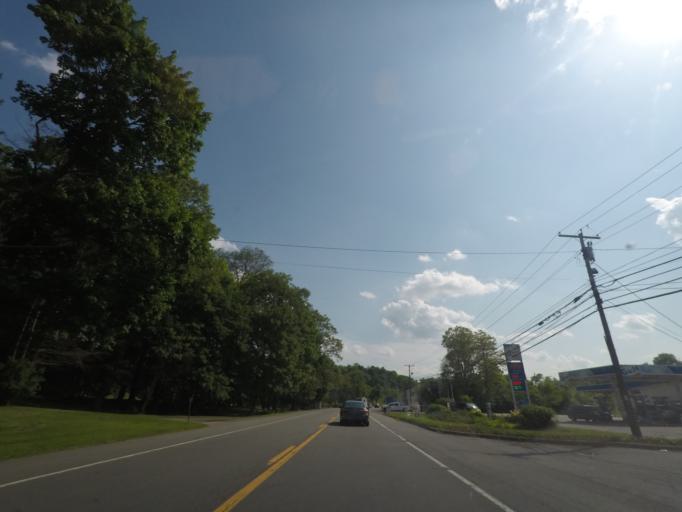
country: US
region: New York
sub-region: Ulster County
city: Marlboro
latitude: 41.5722
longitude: -73.9912
